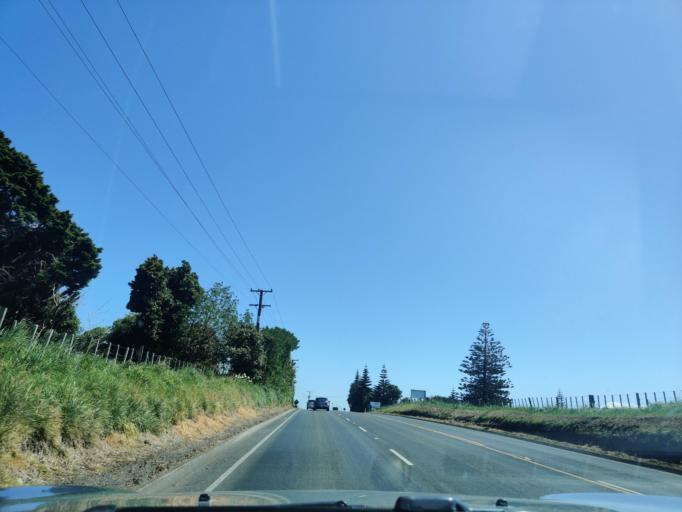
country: NZ
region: Taranaki
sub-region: South Taranaki District
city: Hawera
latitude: -39.6153
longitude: 174.3353
